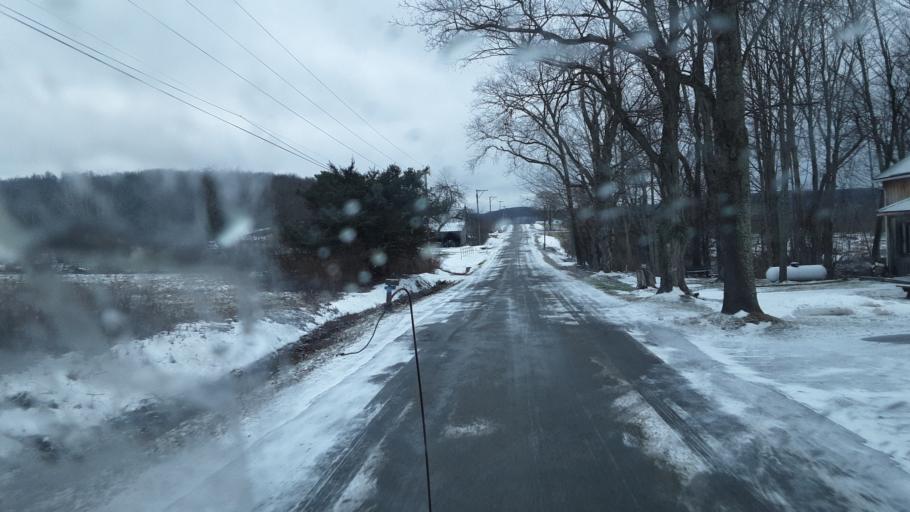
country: US
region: New York
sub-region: Allegany County
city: Friendship
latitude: 42.2938
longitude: -78.1595
